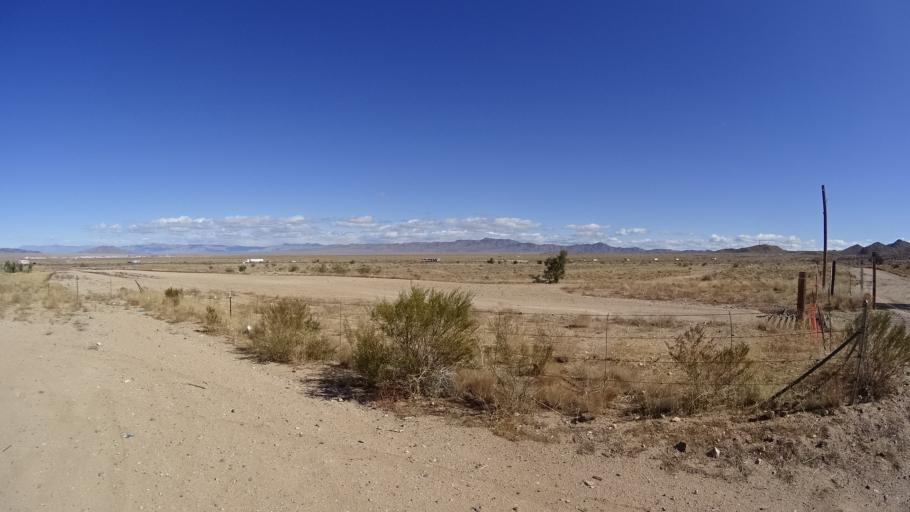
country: US
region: Arizona
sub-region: Mohave County
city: Kingman
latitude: 35.2037
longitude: -113.9589
